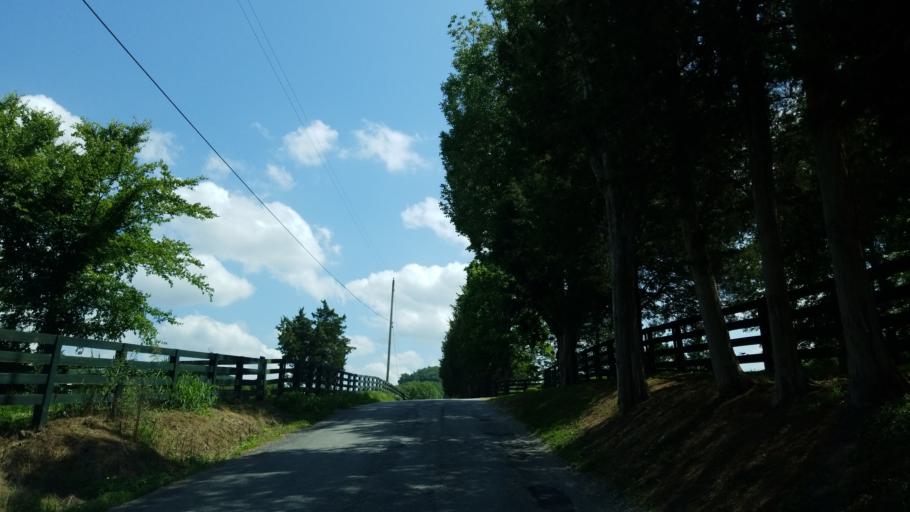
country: US
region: Tennessee
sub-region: Davidson County
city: Forest Hills
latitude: 36.0313
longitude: -86.8635
